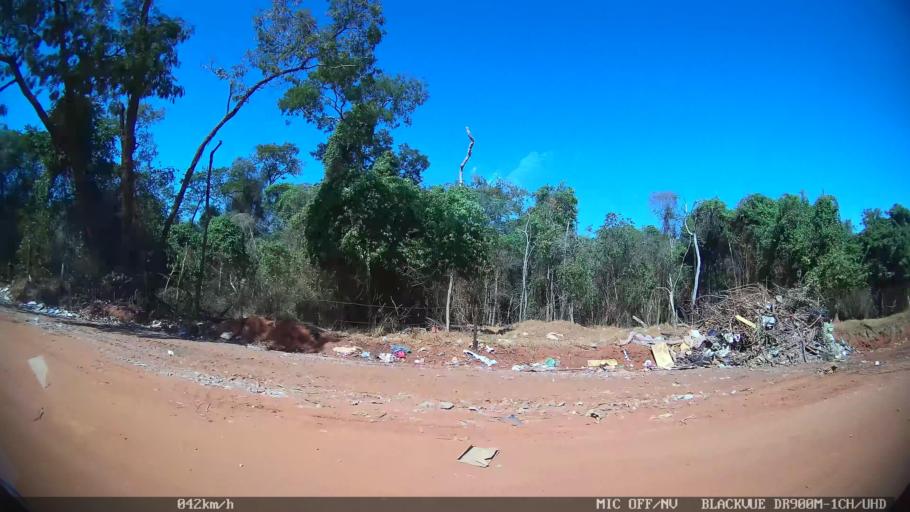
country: BR
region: Sao Paulo
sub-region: Sao Jose Do Rio Preto
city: Sao Jose do Rio Preto
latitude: -20.7425
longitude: -49.4297
